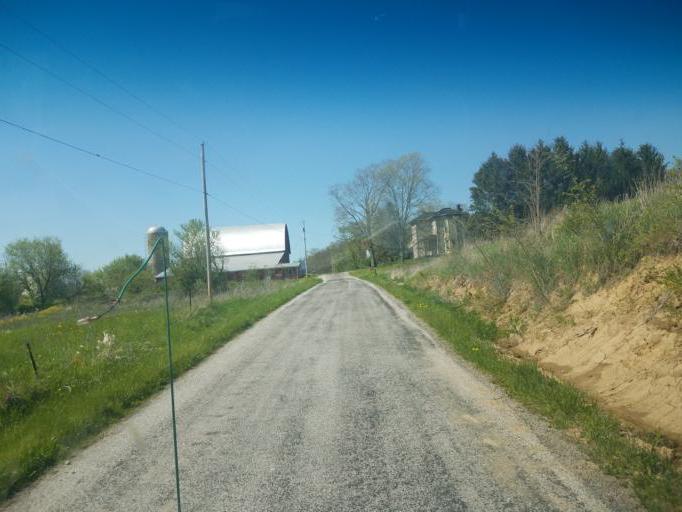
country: US
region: Ohio
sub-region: Medina County
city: Lodi
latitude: 40.9543
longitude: -82.0244
